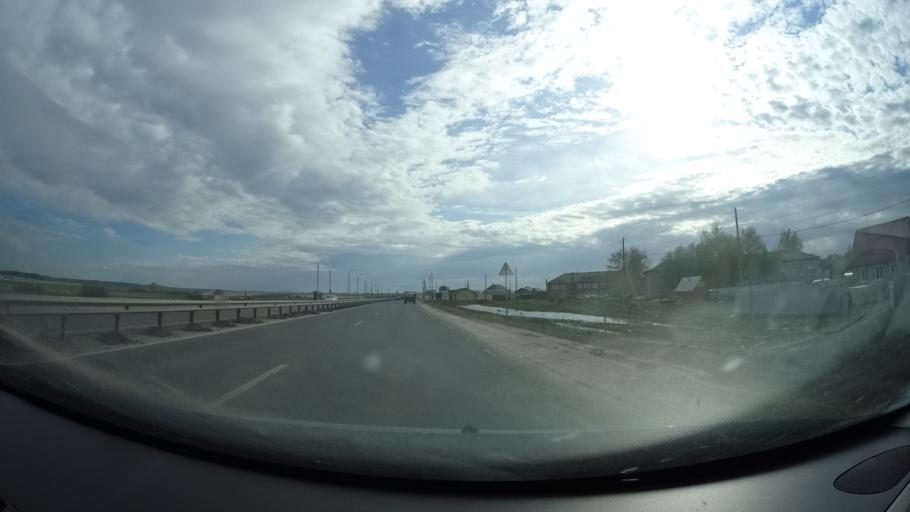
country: RU
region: Perm
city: Kultayevo
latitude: 57.9096
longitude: 55.9922
